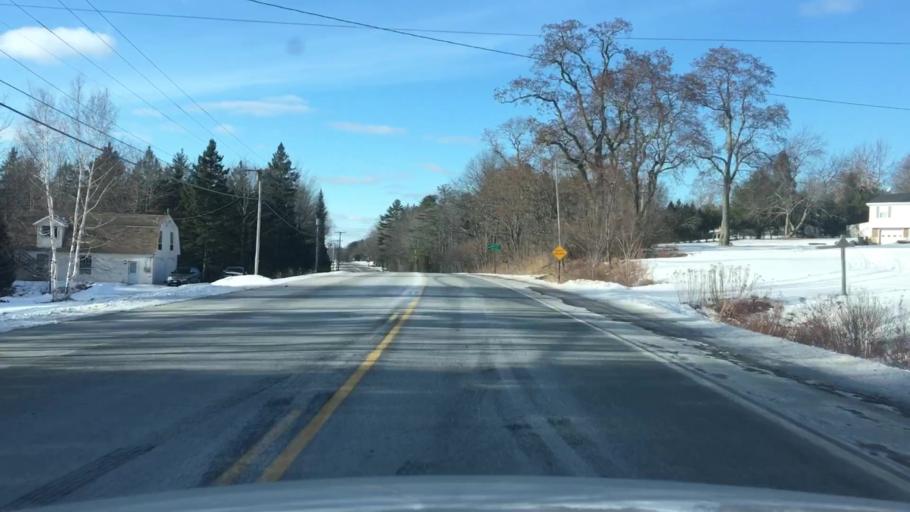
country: US
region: Maine
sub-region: Penobscot County
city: Holden
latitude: 44.8019
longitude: -68.5989
